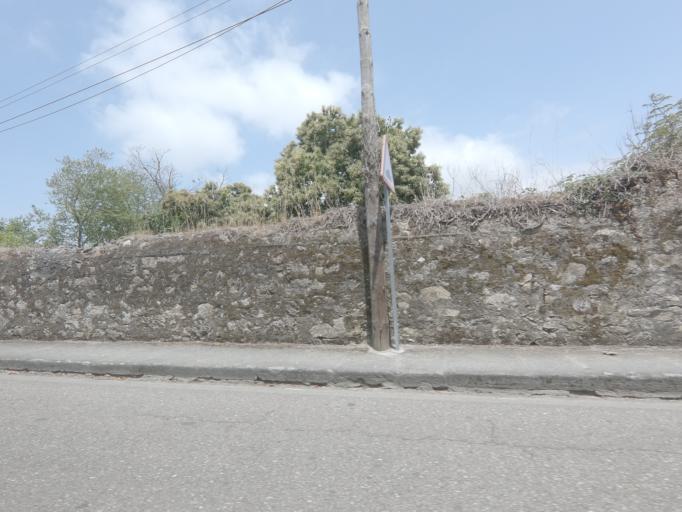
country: ES
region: Galicia
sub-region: Provincia de Pontevedra
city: A Guarda
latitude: 41.8894
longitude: -8.8517
